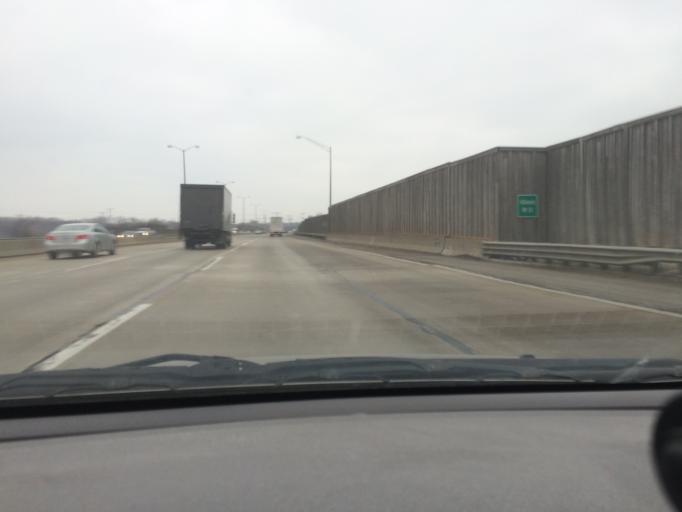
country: US
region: Illinois
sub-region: DuPage County
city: Glen Ellyn
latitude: 41.8650
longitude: -88.0399
